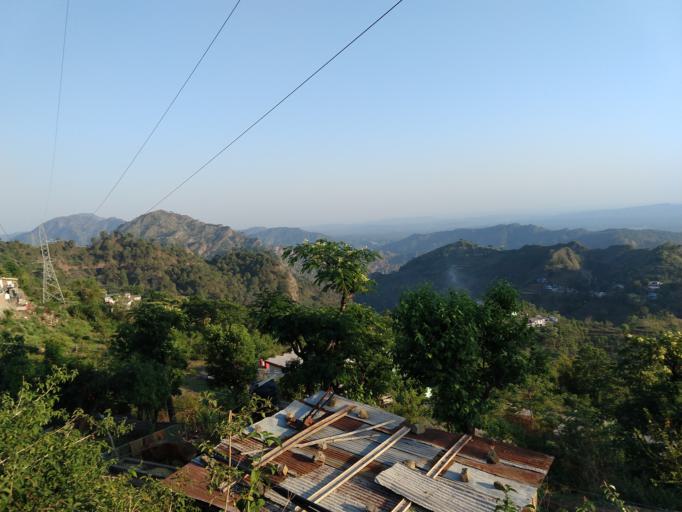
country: IN
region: Punjab
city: Bakloh
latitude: 32.4532
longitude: 75.9344
